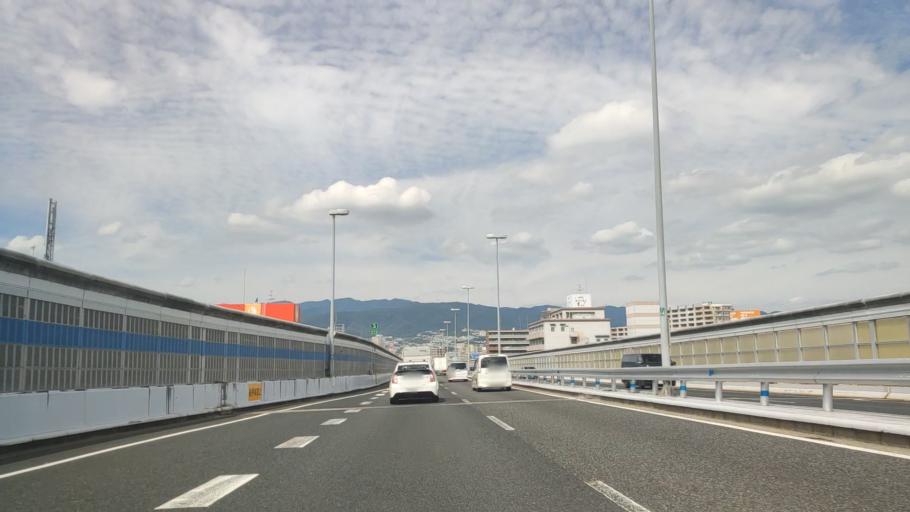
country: JP
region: Hyogo
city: Nishinomiya-hama
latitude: 34.7283
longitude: 135.3524
